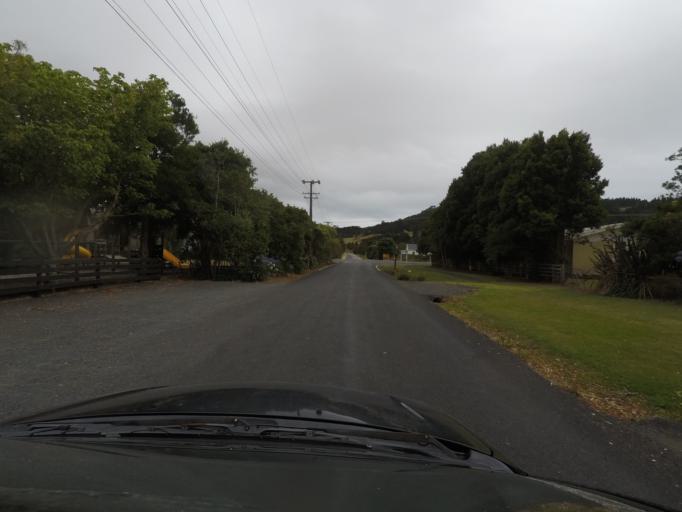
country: NZ
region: Auckland
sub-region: Auckland
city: Warkworth
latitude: -36.2650
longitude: 174.7276
